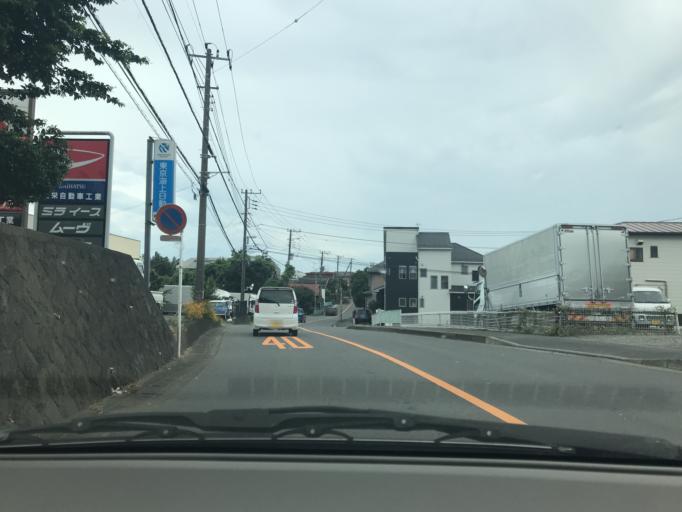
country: JP
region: Kanagawa
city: Fujisawa
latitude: 35.3856
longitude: 139.4391
